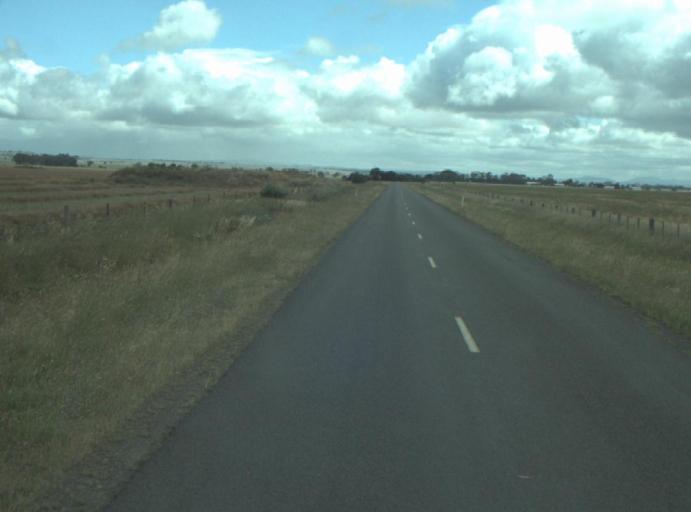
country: AU
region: Victoria
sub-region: Moorabool
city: Bacchus Marsh
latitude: -37.8322
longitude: 144.3570
